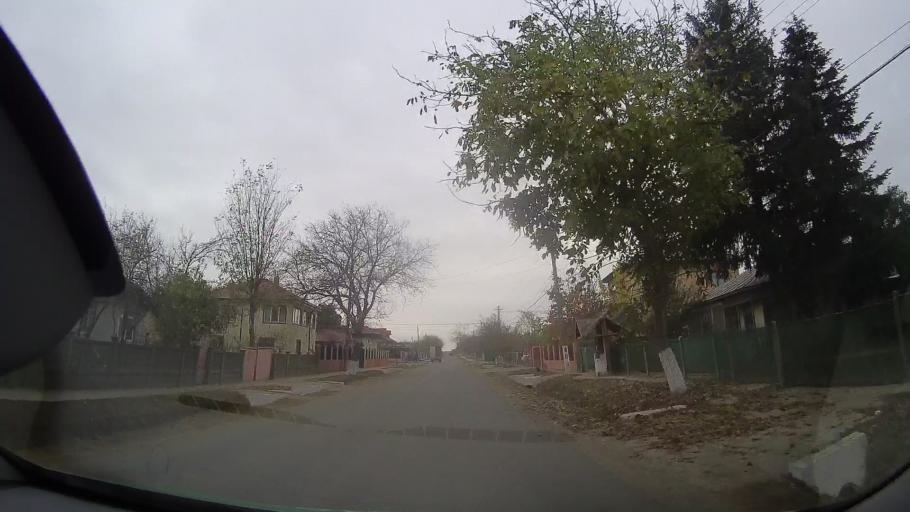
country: RO
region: Buzau
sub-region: Comuna Rusetu
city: Rusetu
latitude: 44.9639
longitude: 27.2104
